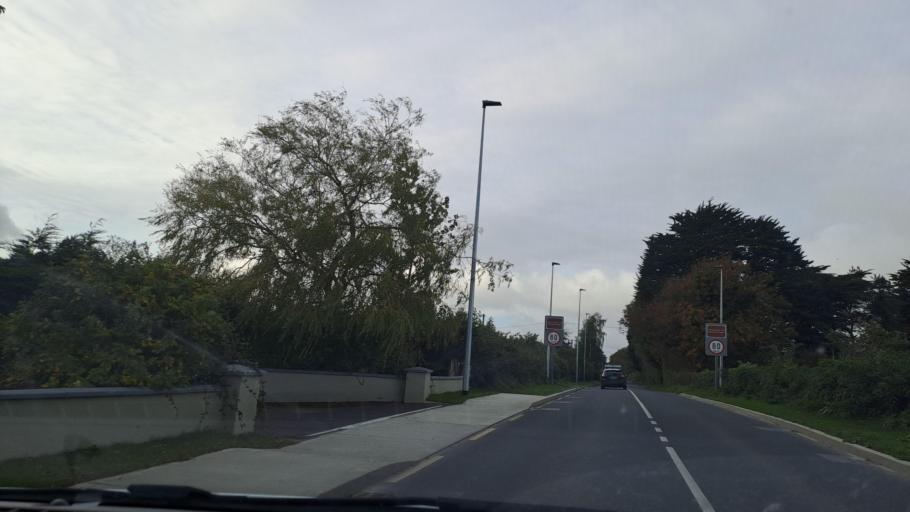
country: IE
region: Leinster
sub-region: An Mhi
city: Navan
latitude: 53.7077
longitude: -6.6868
